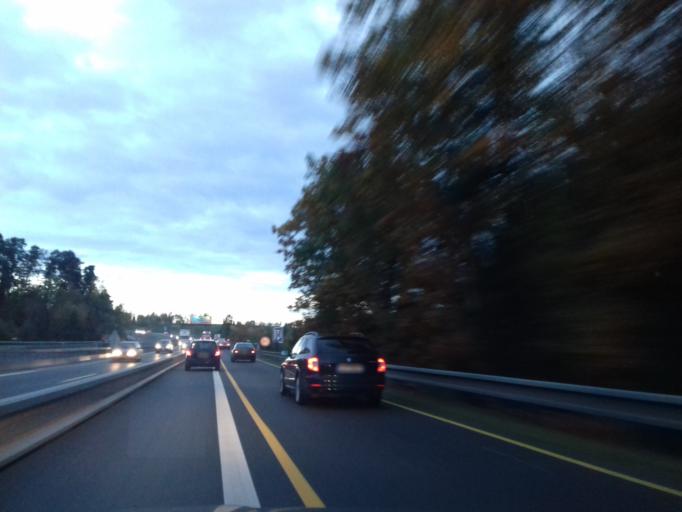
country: CZ
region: Central Bohemia
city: Trhovy Stepanov
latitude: 49.7476
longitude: 15.0292
